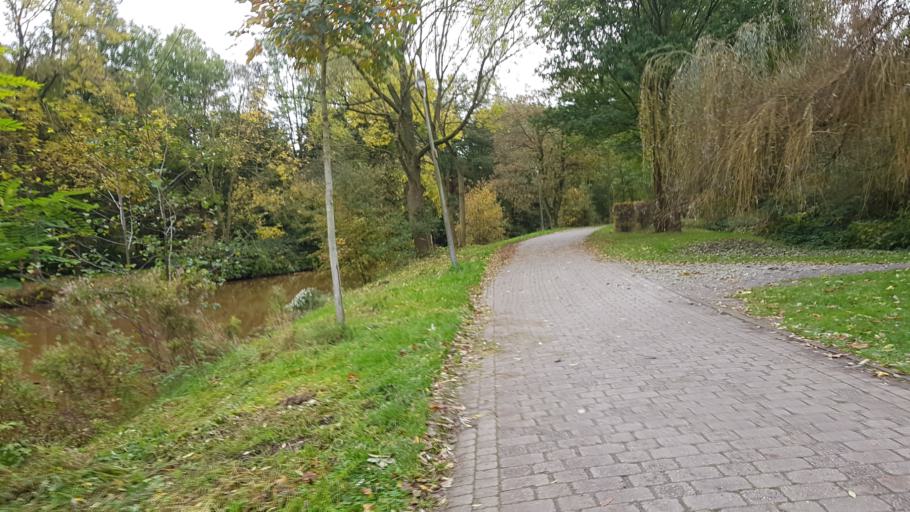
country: DE
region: Bremen
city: Bremen
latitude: 53.1013
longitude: 8.8265
